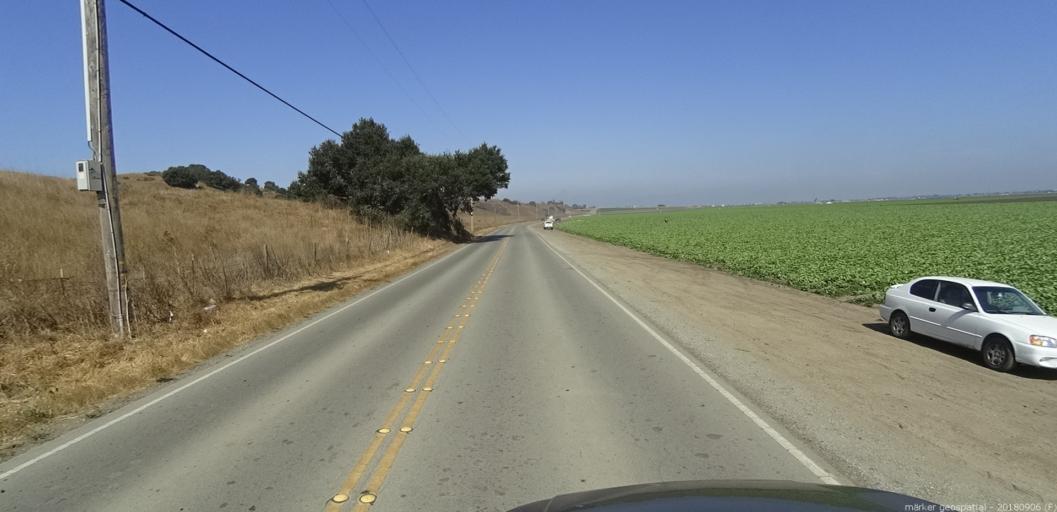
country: US
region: California
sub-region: Monterey County
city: Chualar
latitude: 36.5764
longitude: -121.5872
